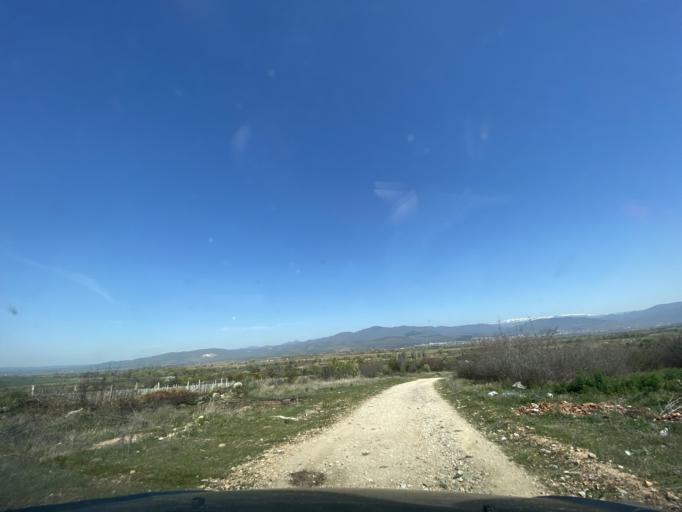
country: MK
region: Zrnovci
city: Zrnovci
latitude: 41.8515
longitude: 22.3894
